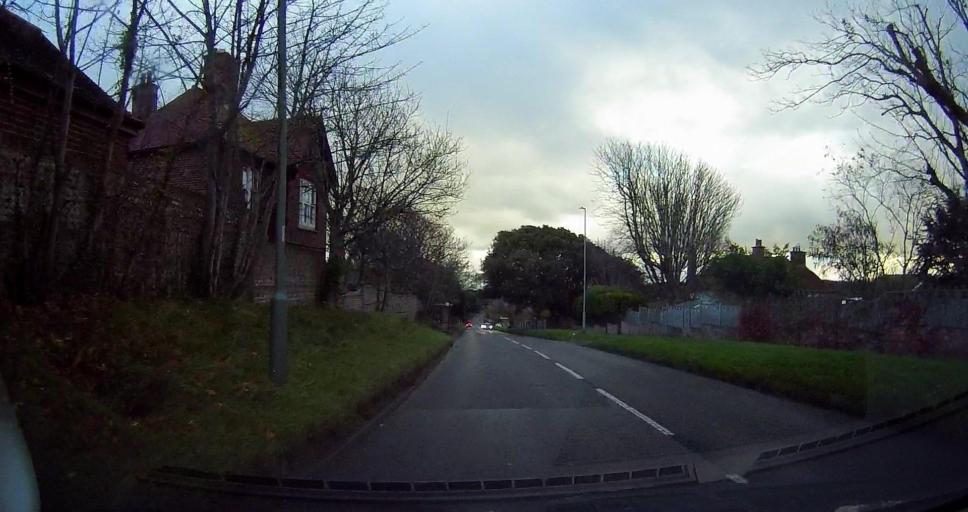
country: GB
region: England
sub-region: Brighton and Hove
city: Rottingdean
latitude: 50.8163
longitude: -0.0640
